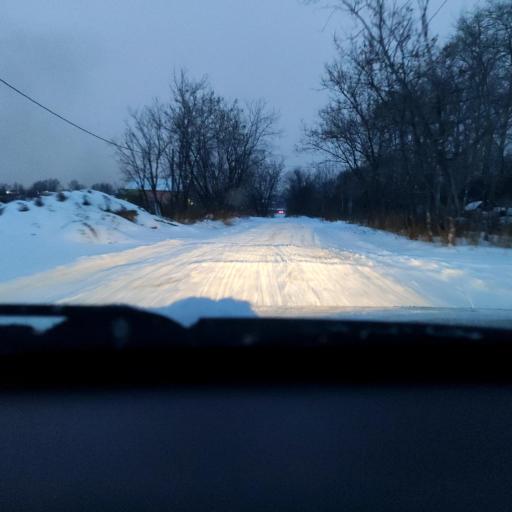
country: RU
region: Perm
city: Froly
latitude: 57.9483
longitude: 56.2312
